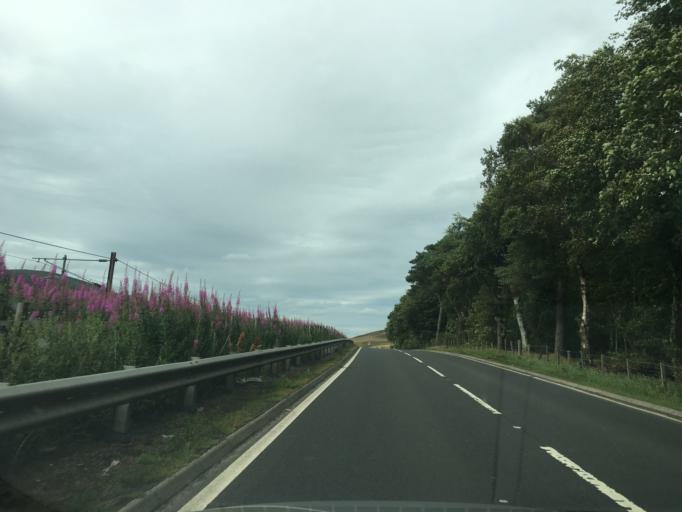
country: GB
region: Scotland
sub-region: South Lanarkshire
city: Biggar
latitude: 55.5270
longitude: -3.6714
